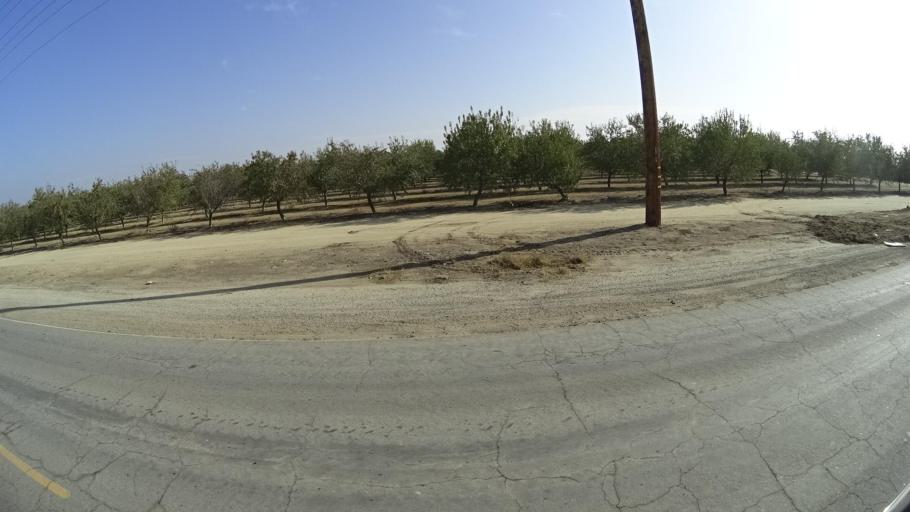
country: US
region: California
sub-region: Kern County
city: Delano
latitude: 35.7548
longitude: -119.2233
